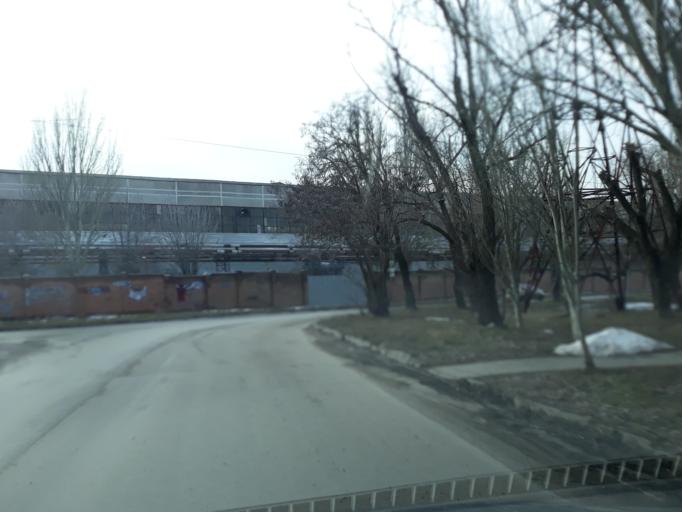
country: RU
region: Rostov
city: Taganrog
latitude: 47.2505
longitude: 38.9052
